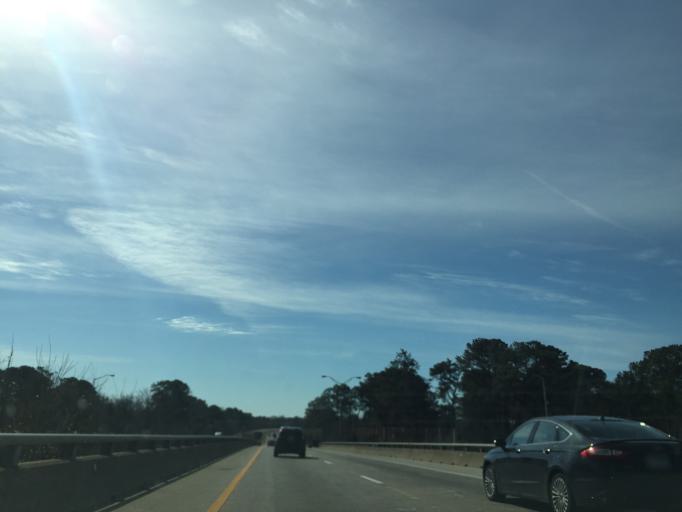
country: US
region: Virginia
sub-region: City of Norfolk
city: Norfolk
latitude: 36.9431
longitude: -76.2666
